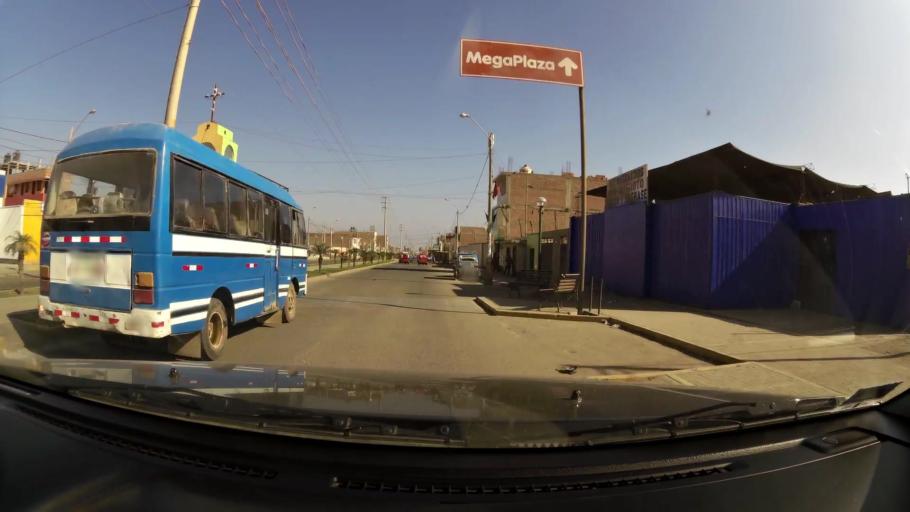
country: PE
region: Ica
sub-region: Provincia de Chincha
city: Chincha Alta
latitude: -13.4047
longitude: -76.1298
